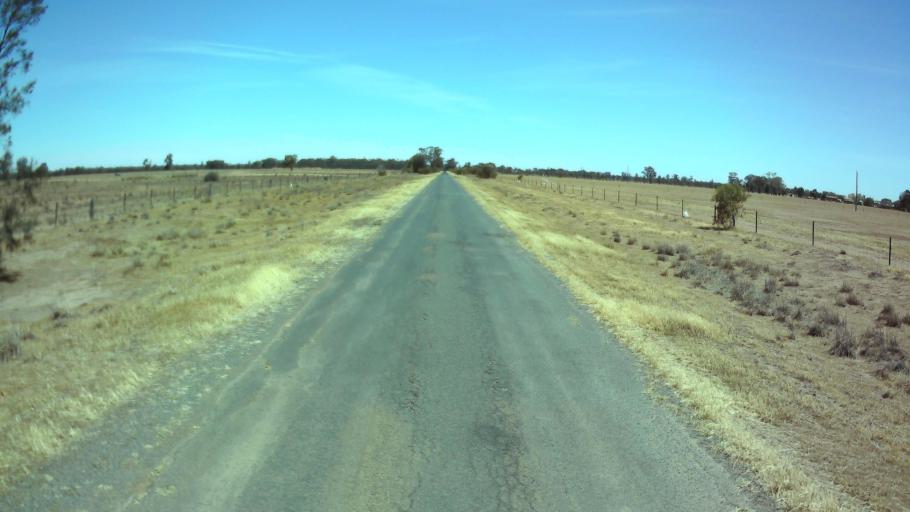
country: AU
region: New South Wales
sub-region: Weddin
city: Grenfell
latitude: -33.8902
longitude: 147.6883
